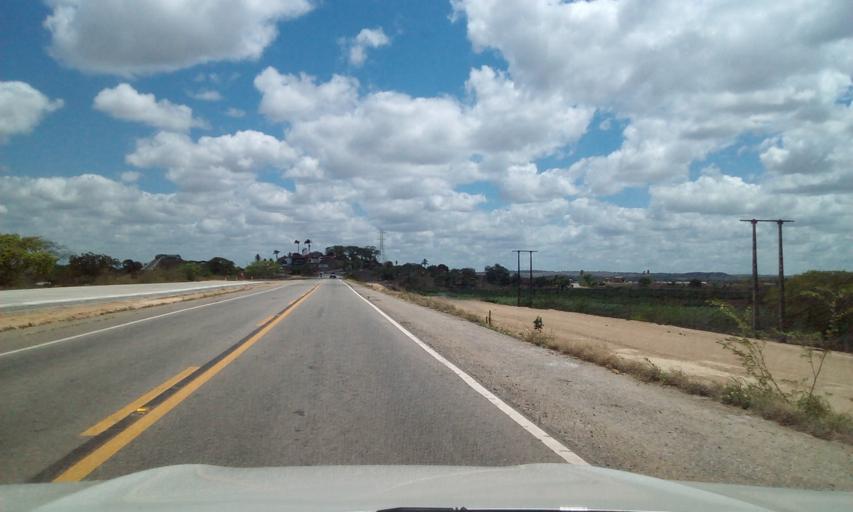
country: BR
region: Sergipe
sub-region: Propria
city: Propria
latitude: -10.2196
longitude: -36.8271
